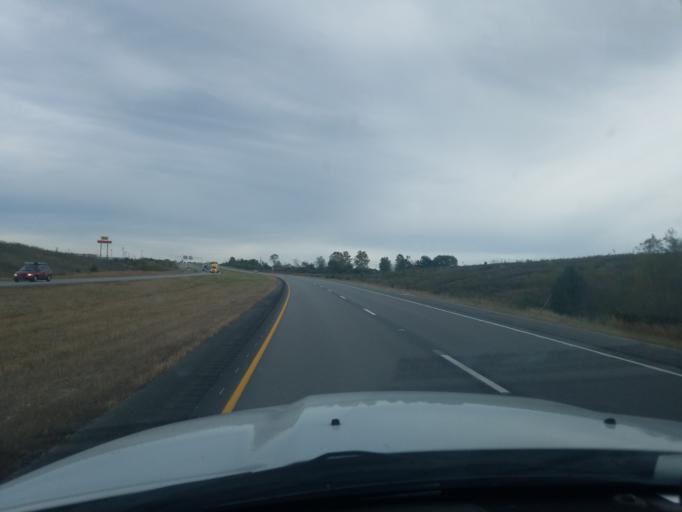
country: US
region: Indiana
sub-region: Spencer County
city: Dale
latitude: 38.1938
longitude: -86.9803
